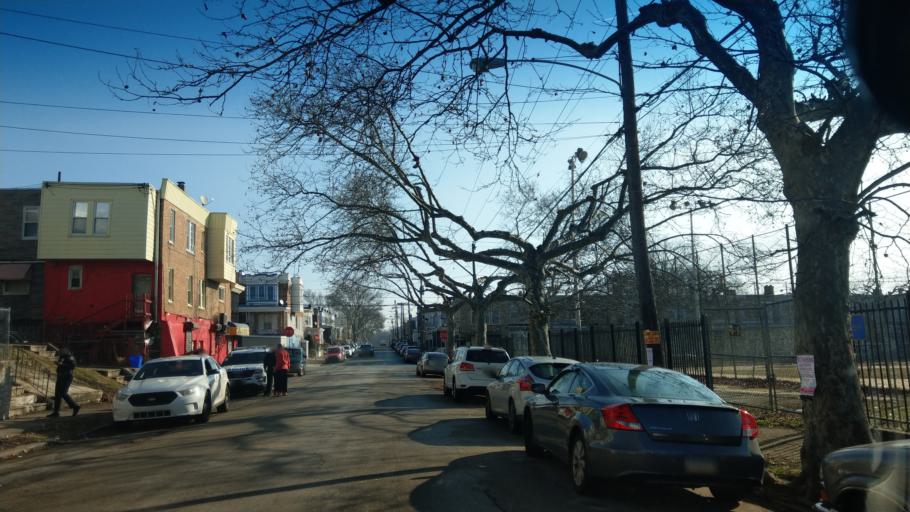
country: US
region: Pennsylvania
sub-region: Montgomery County
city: Rockledge
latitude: 40.0227
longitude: -75.1209
